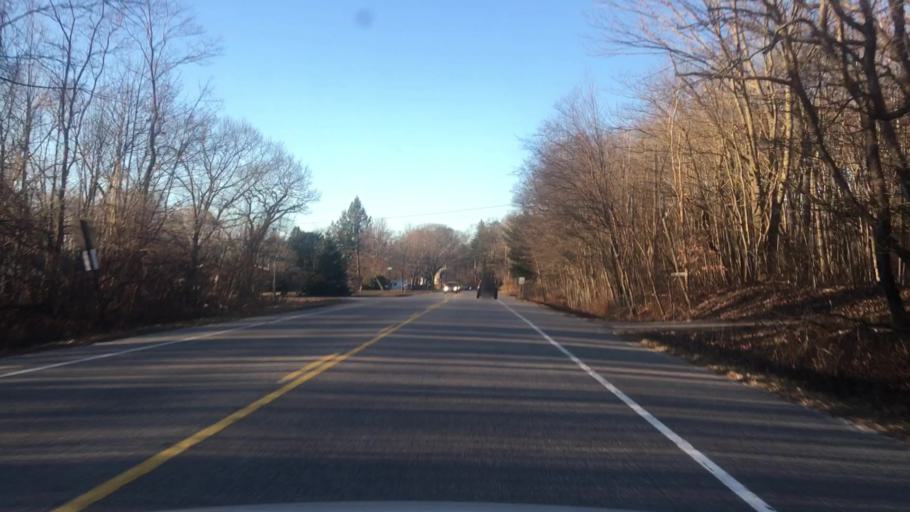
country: US
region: Maine
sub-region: York County
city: South Eliot
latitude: 43.1041
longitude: -70.7611
